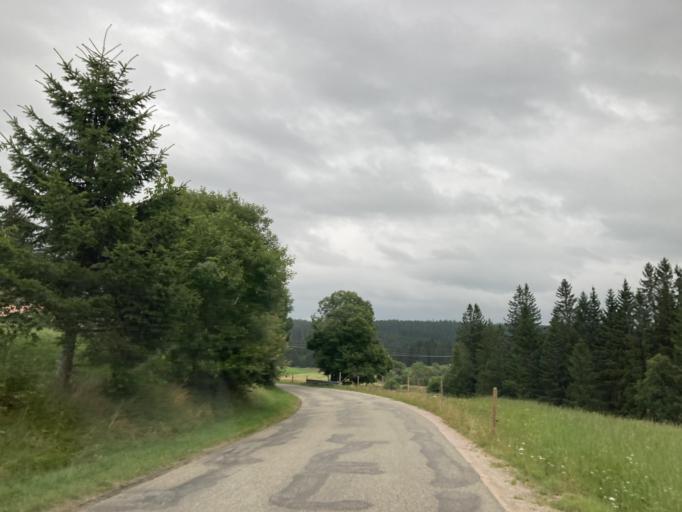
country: DE
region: Baden-Wuerttemberg
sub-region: Freiburg Region
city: Schonwald im Schwarzwald
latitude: 48.1189
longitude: 8.2026
